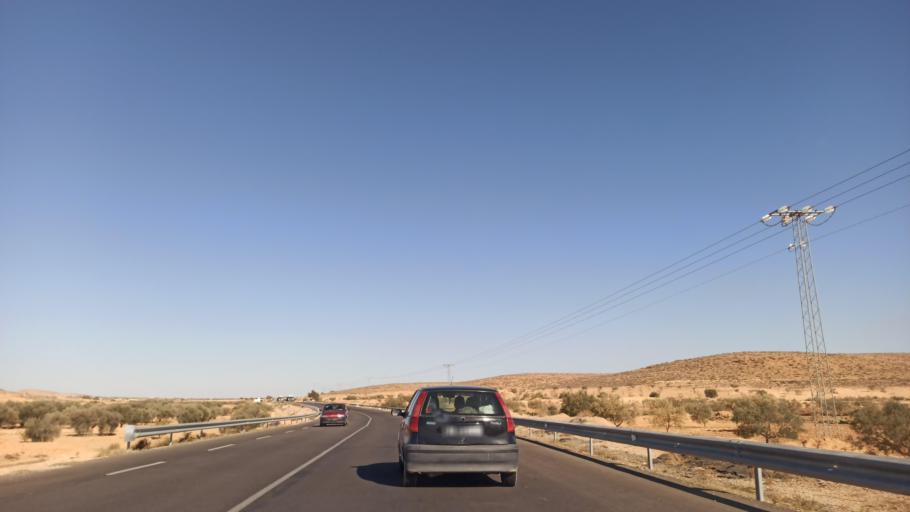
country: TN
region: Sidi Bu Zayd
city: Bi'r al Hufayy
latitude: 34.7181
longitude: 9.0589
